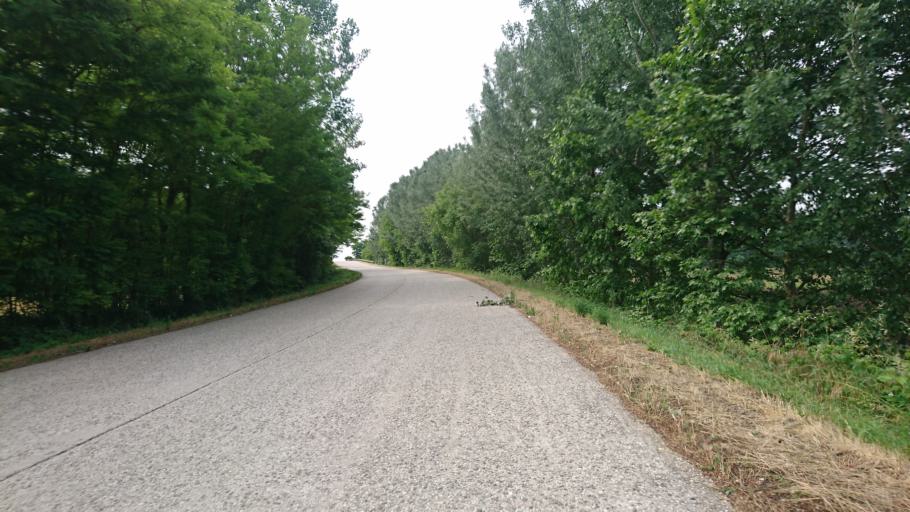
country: IT
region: Veneto
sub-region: Provincia di Padova
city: Monselice
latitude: 45.2299
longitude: 11.7200
